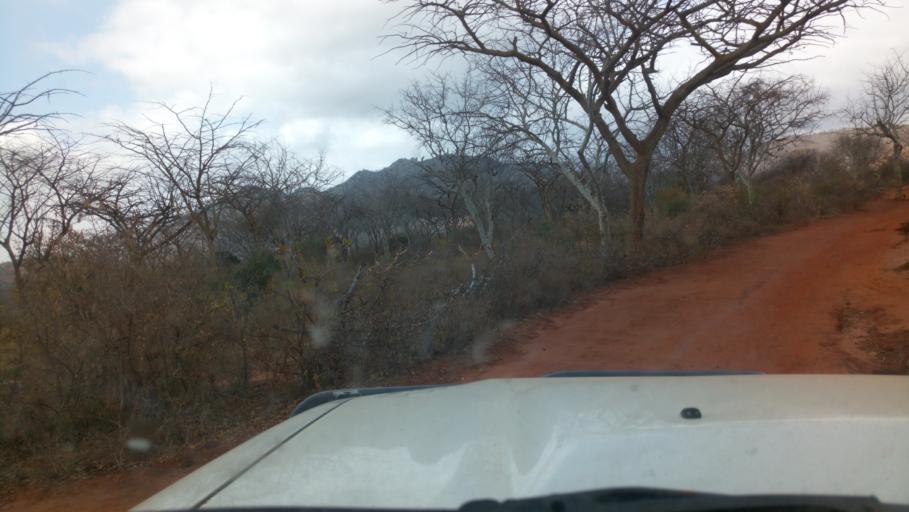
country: KE
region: Kitui
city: Kitui
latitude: -1.8470
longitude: 38.3368
